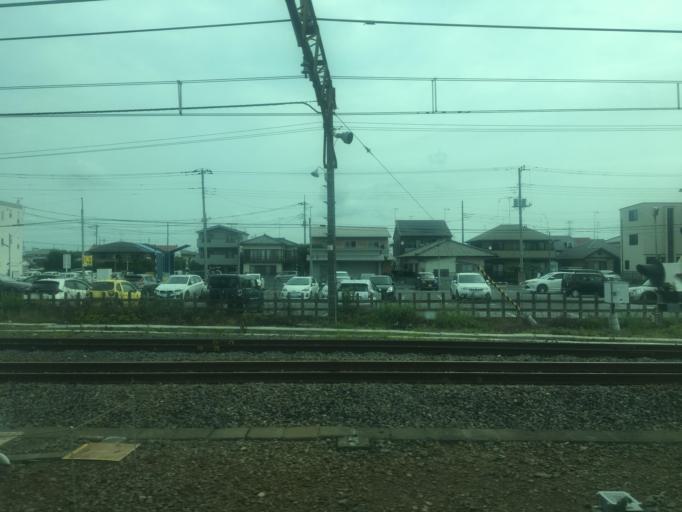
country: JP
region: Saitama
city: Fukayacho
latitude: 36.1736
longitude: 139.3322
